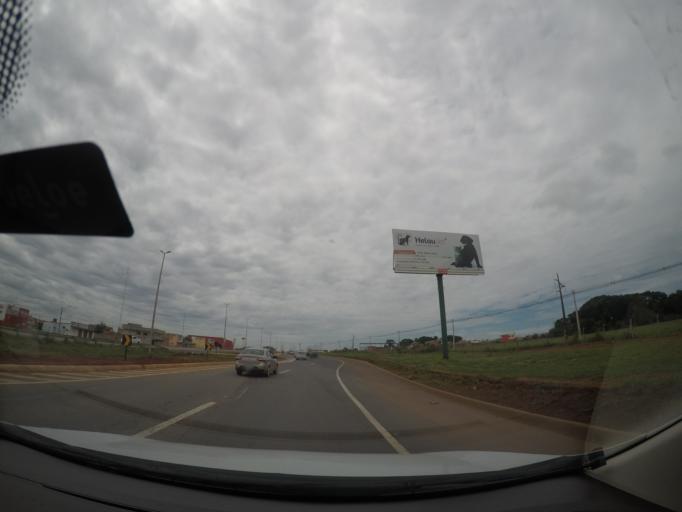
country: BR
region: Goias
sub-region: Goianira
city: Goianira
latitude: -16.5756
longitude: -49.3916
